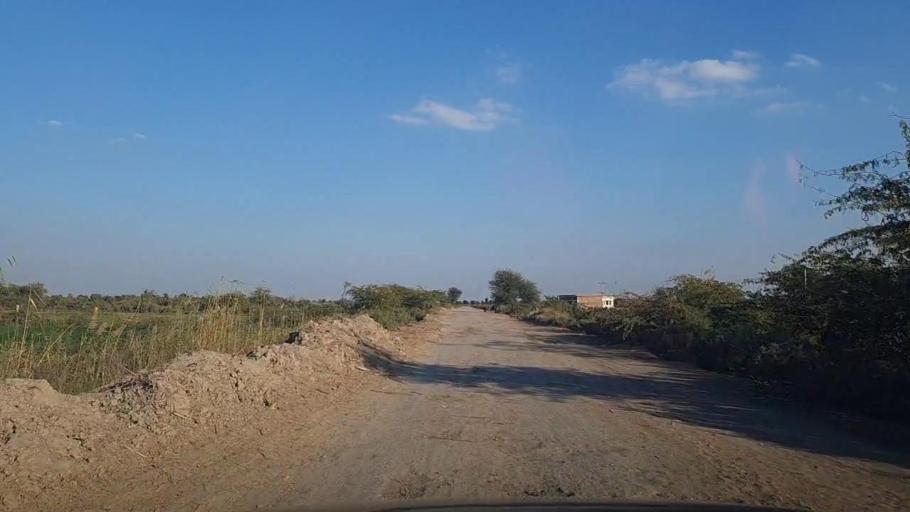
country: PK
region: Sindh
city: Jhol
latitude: 25.9245
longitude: 69.0214
